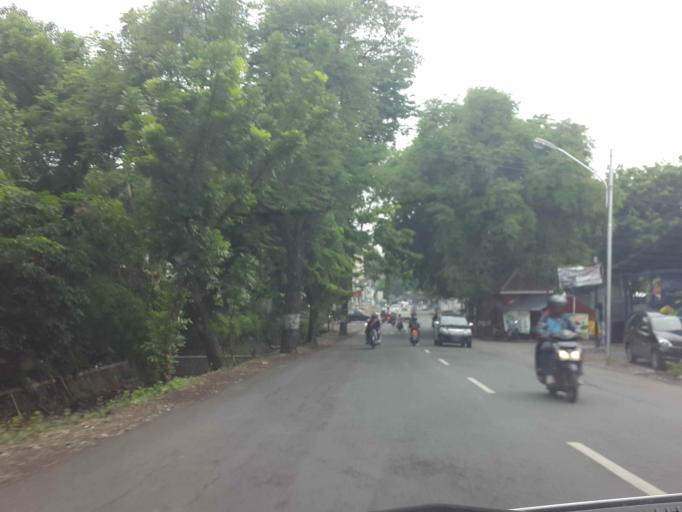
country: ID
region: Central Java
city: Semarang
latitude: -7.0002
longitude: 110.4231
